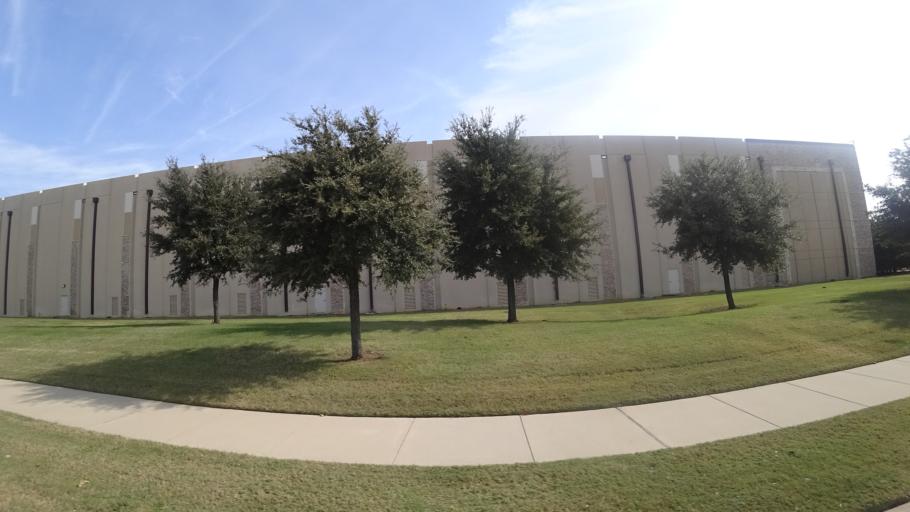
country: US
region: Texas
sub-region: Denton County
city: The Colony
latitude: 33.0635
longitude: -96.8713
